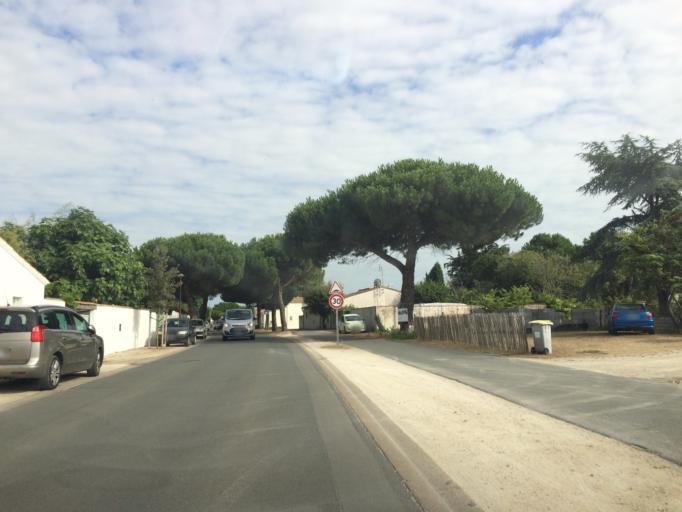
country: FR
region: Poitou-Charentes
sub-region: Departement de la Charente-Maritime
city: La Flotte
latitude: 46.1864
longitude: -1.3333
